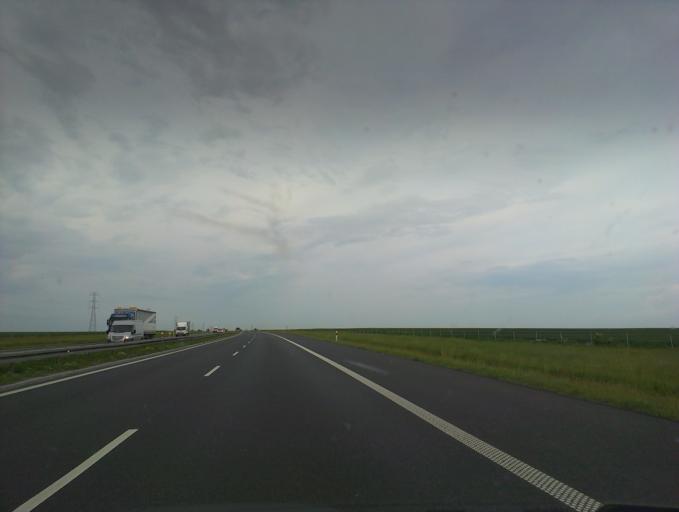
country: PL
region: Opole Voivodeship
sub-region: Powiat brzeski
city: Olszanka
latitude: 50.7379
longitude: 17.4726
